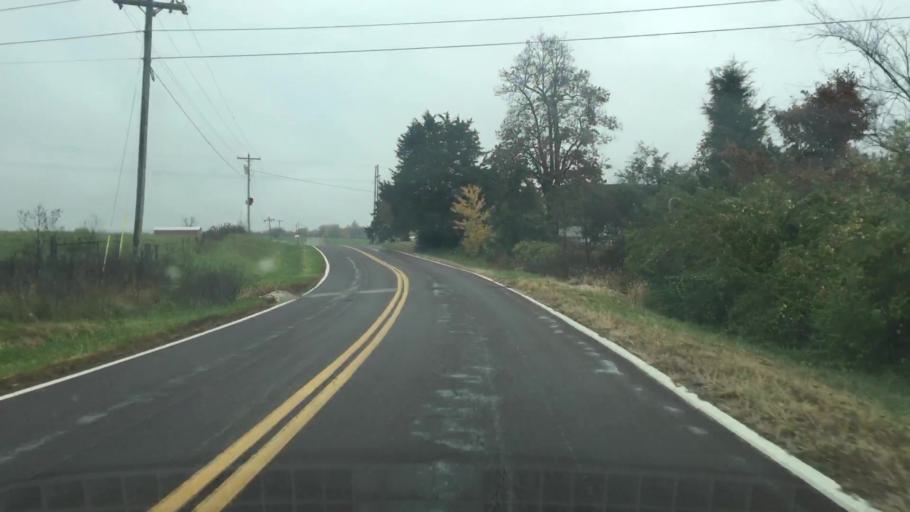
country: US
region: Missouri
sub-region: Callaway County
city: Fulton
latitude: 38.8334
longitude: -91.9194
